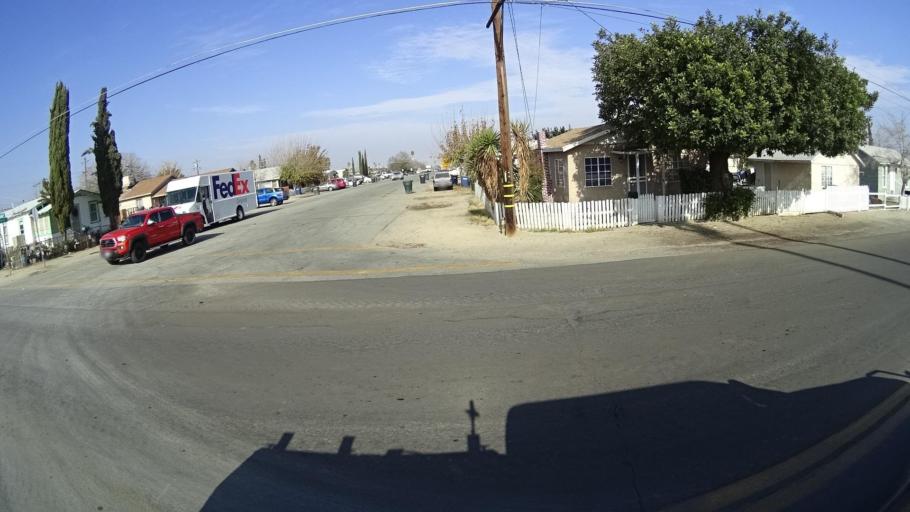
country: US
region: California
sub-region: Kern County
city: Ford City
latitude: 35.1549
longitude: -119.4600
